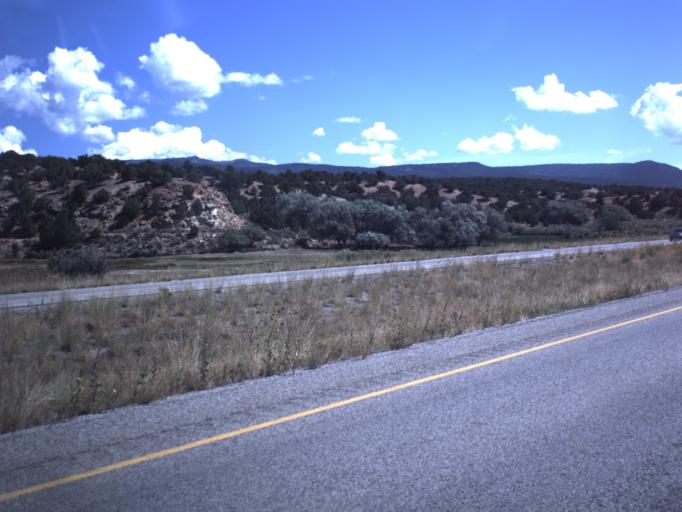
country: US
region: Utah
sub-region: Sevier County
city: Salina
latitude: 38.9188
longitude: -111.7507
